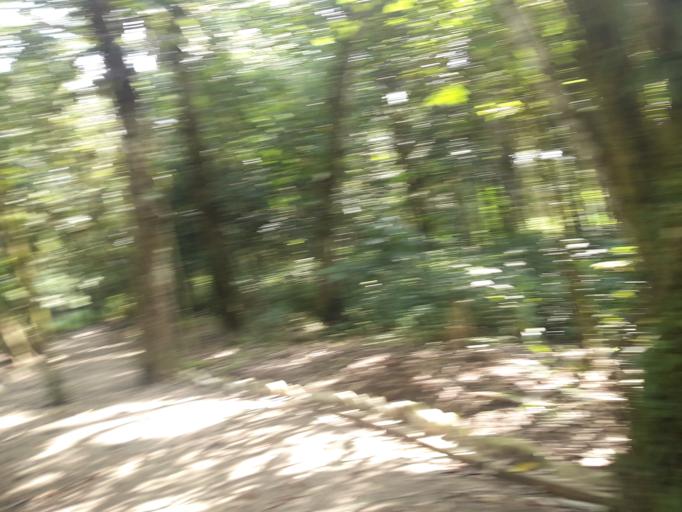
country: EC
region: Napo
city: Tena
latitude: -0.9945
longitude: -77.8174
